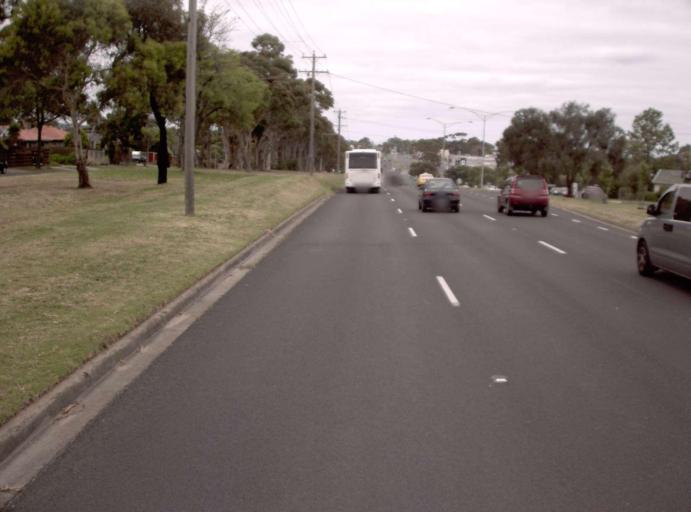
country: AU
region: Victoria
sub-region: Mornington Peninsula
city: Mornington
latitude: -38.2240
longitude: 145.0522
